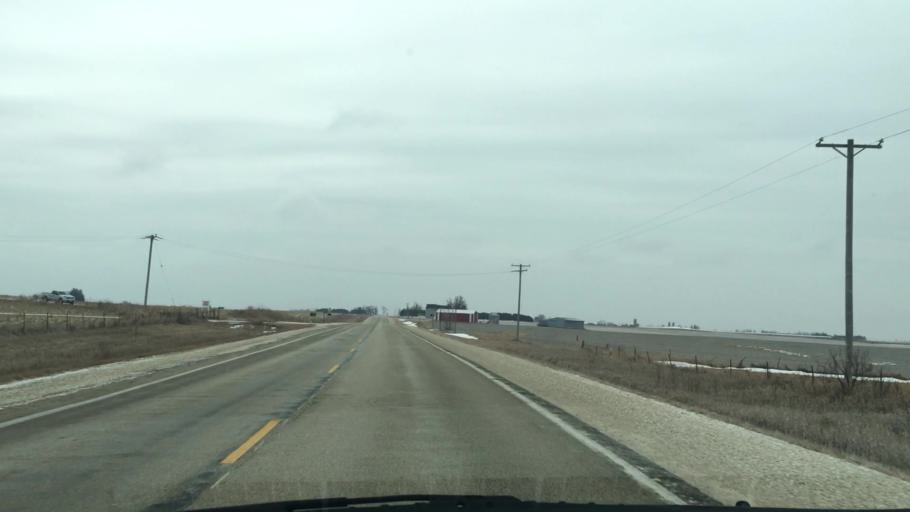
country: US
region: Iowa
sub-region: Fayette County
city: West Union
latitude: 43.0322
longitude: -91.8357
